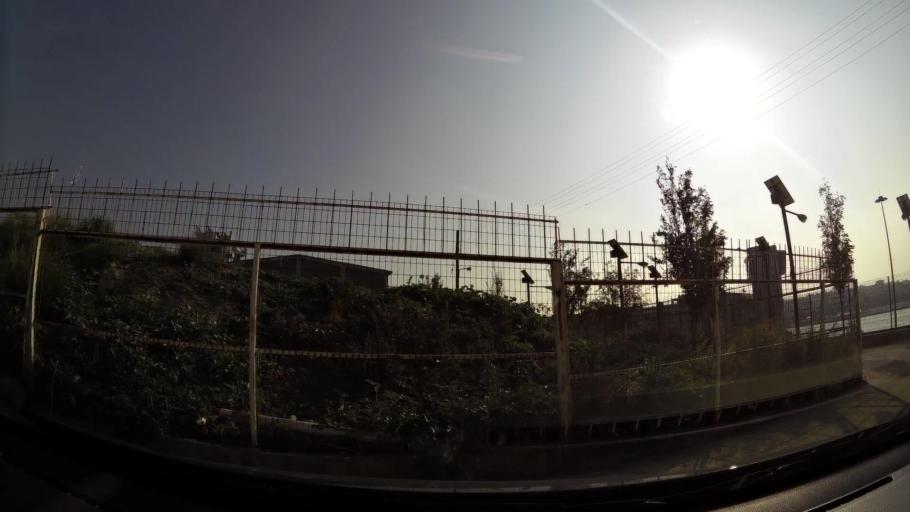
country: GR
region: Attica
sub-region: Nomos Piraios
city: Drapetsona
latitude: 37.9438
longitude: 23.6244
